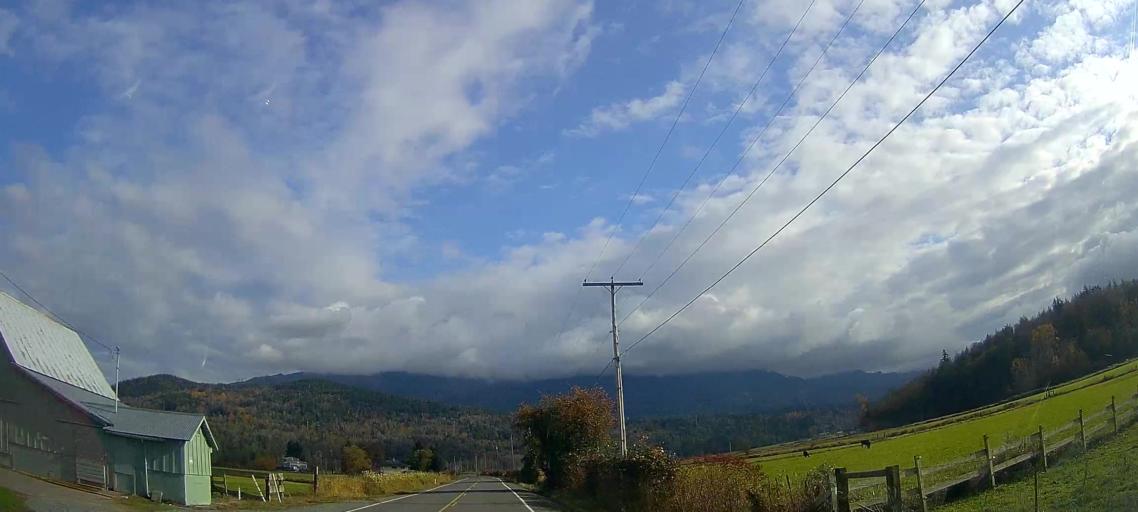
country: US
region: Washington
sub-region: Skagit County
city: Clear Lake
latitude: 48.4524
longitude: -122.2305
